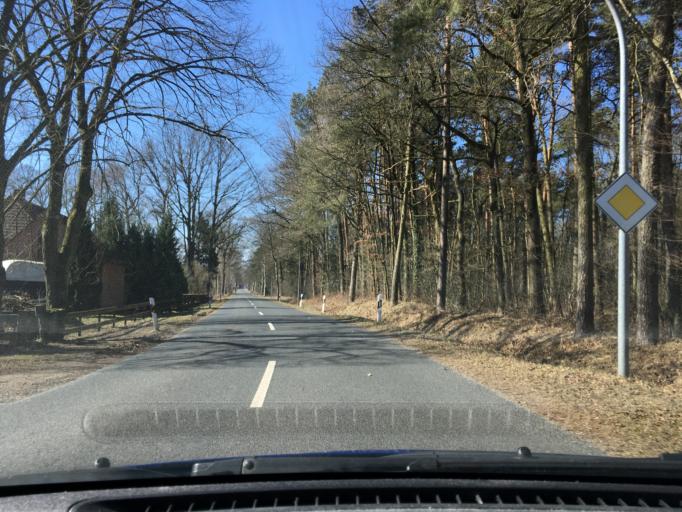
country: DE
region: Lower Saxony
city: Neuenkirchen
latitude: 53.0707
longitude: 9.6801
